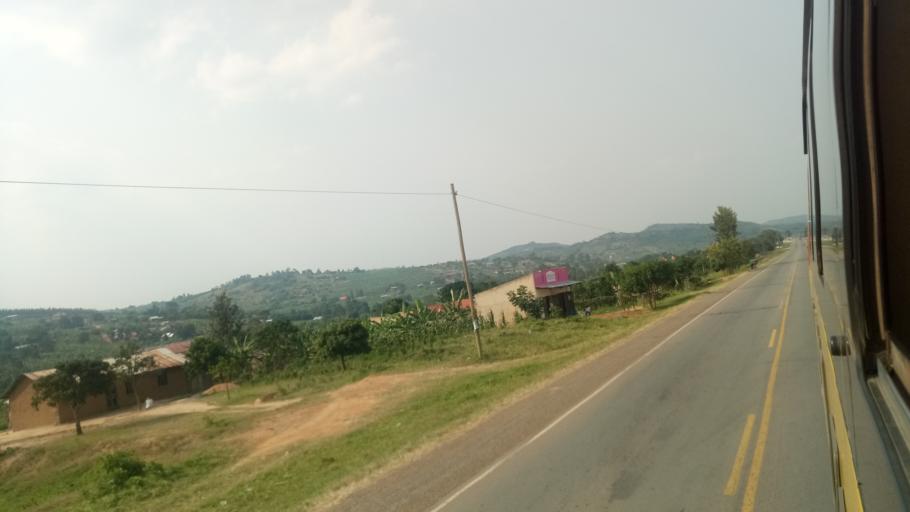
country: UG
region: Western Region
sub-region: Mbarara District
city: Mbarara
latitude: -0.5287
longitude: 30.7236
